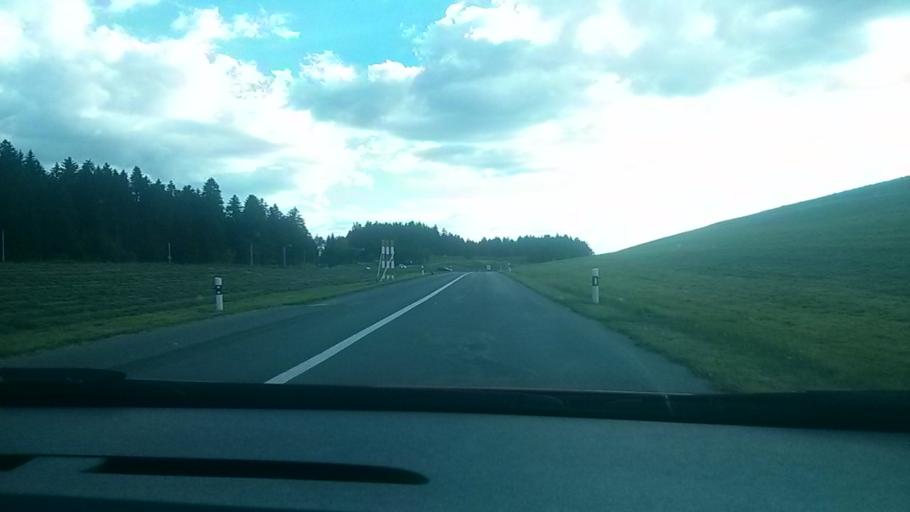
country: CH
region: Vaud
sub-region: Jura-Nord vaudois District
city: L'Abbaye
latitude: 46.6422
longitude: 6.2741
